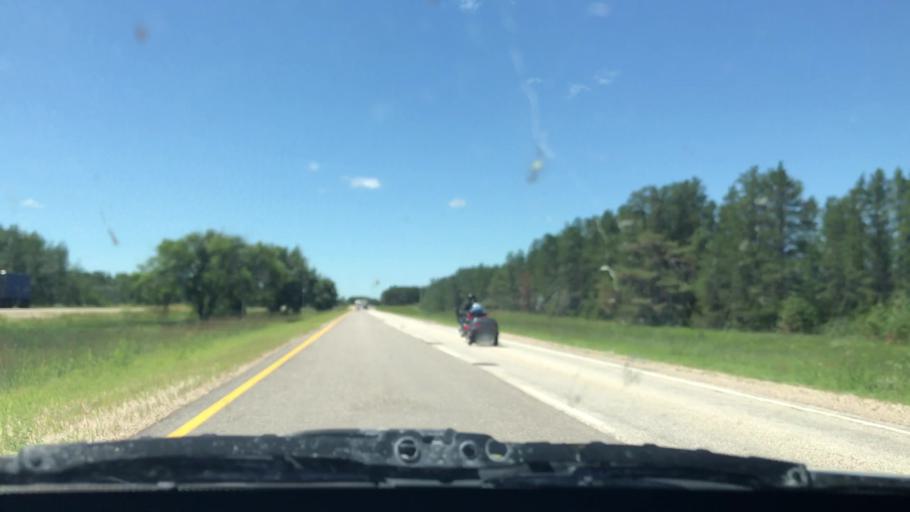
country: CA
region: Manitoba
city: La Broquerie
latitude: 49.6561
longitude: -96.1539
